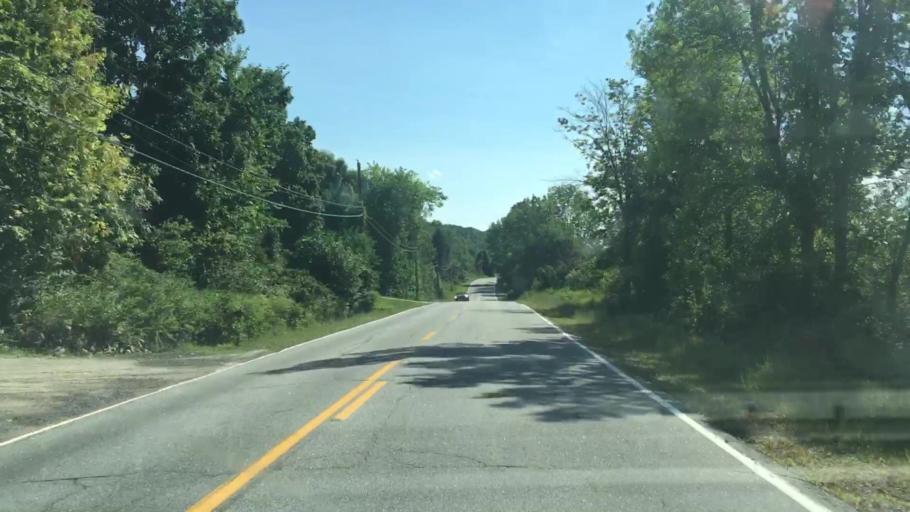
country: US
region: Maine
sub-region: Androscoggin County
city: Sabattus
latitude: 44.1533
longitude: -70.0810
